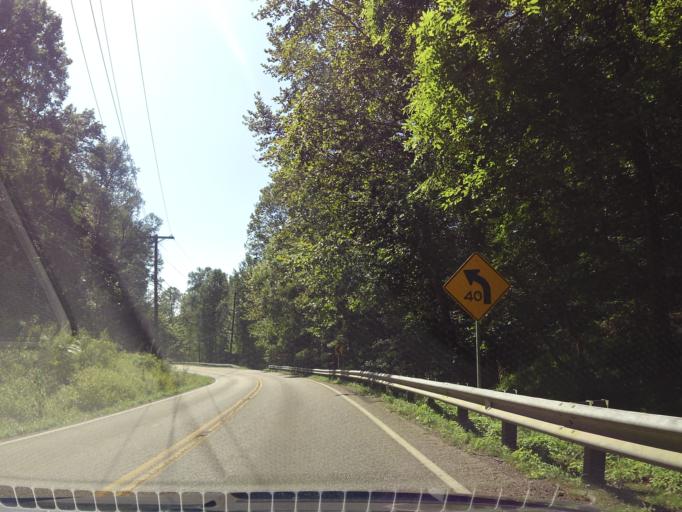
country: US
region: Kentucky
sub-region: Clay County
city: Manchester
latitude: 37.1110
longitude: -83.7184
